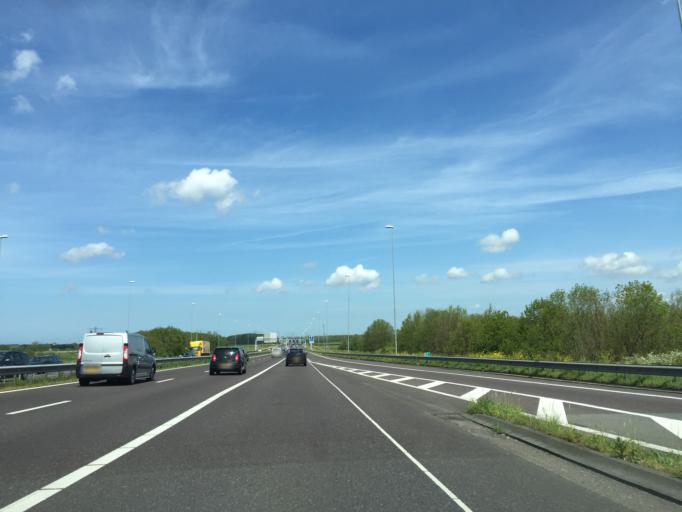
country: NL
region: North Holland
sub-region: Gemeente Haarlem
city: Haarlem
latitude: 52.3885
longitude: 4.7070
